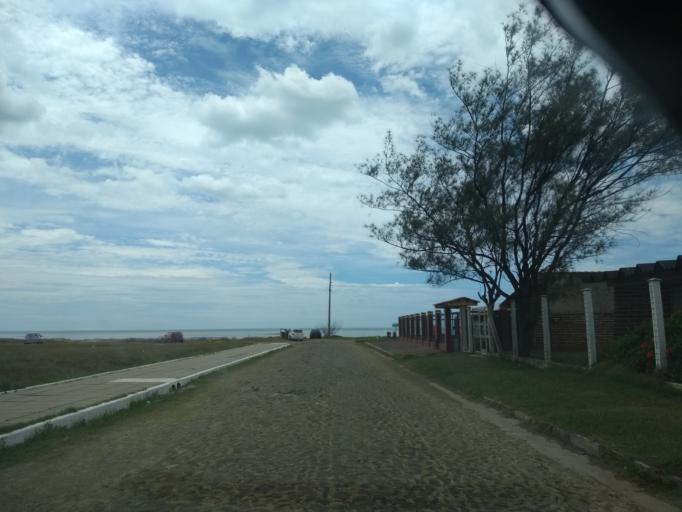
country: BR
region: Rio Grande do Sul
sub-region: Tramandai
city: Tramandai
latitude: -30.0642
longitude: -50.1591
